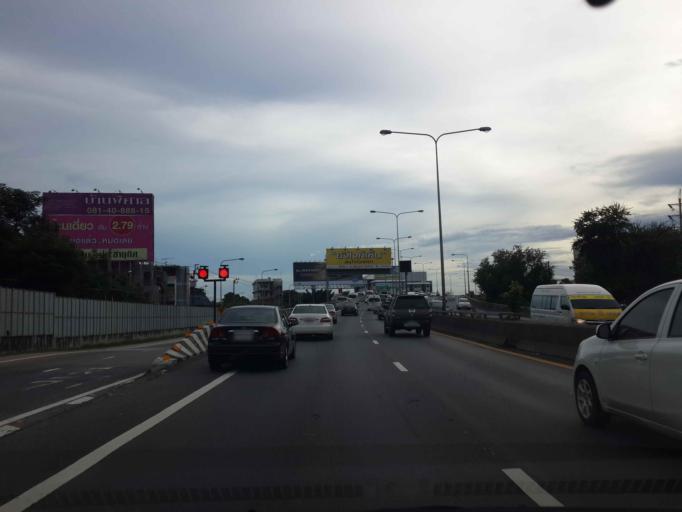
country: TH
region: Bangkok
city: Rat Burana
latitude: 13.6734
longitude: 100.5107
